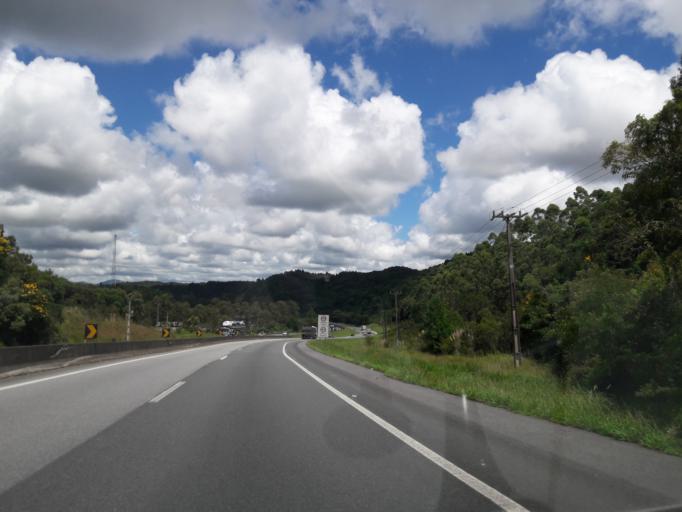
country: BR
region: Parana
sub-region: Campina Grande Do Sul
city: Campina Grande do Sul
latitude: -25.2468
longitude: -48.9046
